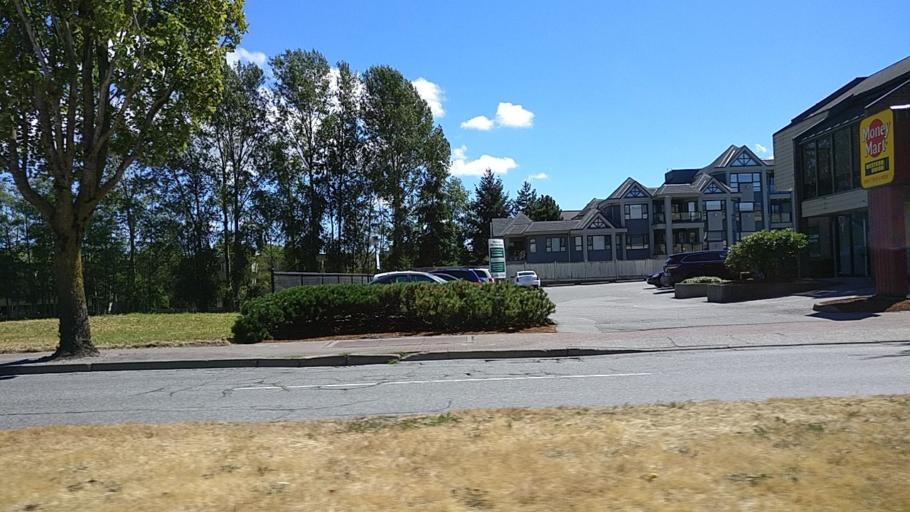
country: CA
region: British Columbia
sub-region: Greater Vancouver Regional District
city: White Rock
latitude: 49.0355
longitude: -122.8013
